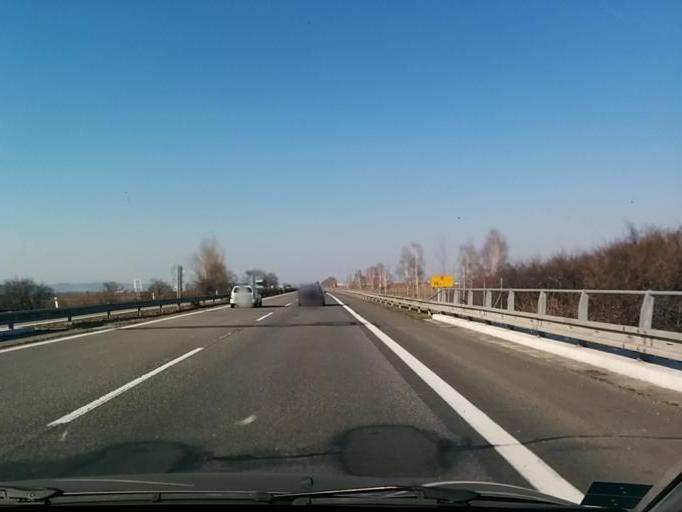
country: SK
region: Trnavsky
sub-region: Okres Trnava
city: Piestany
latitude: 48.5557
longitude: 17.7890
